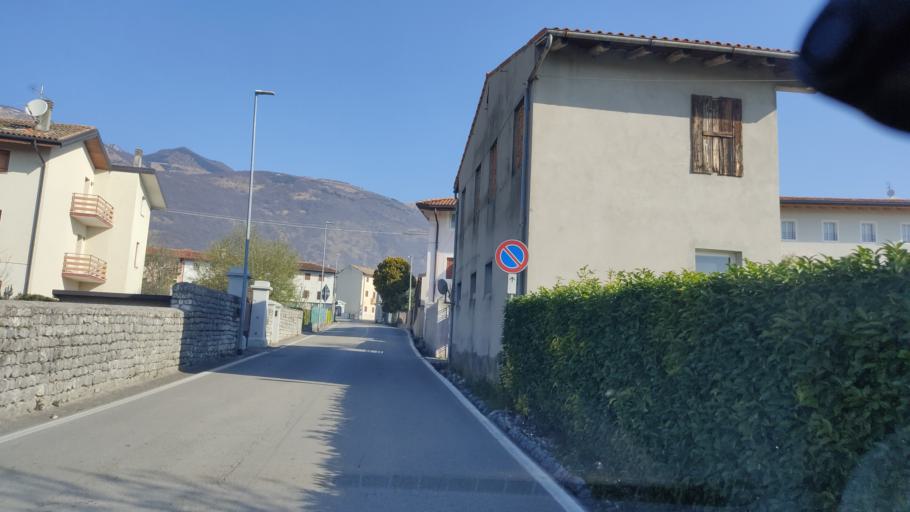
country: IT
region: Friuli Venezia Giulia
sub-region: Provincia di Pordenone
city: Budoia
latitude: 46.0502
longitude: 12.5339
